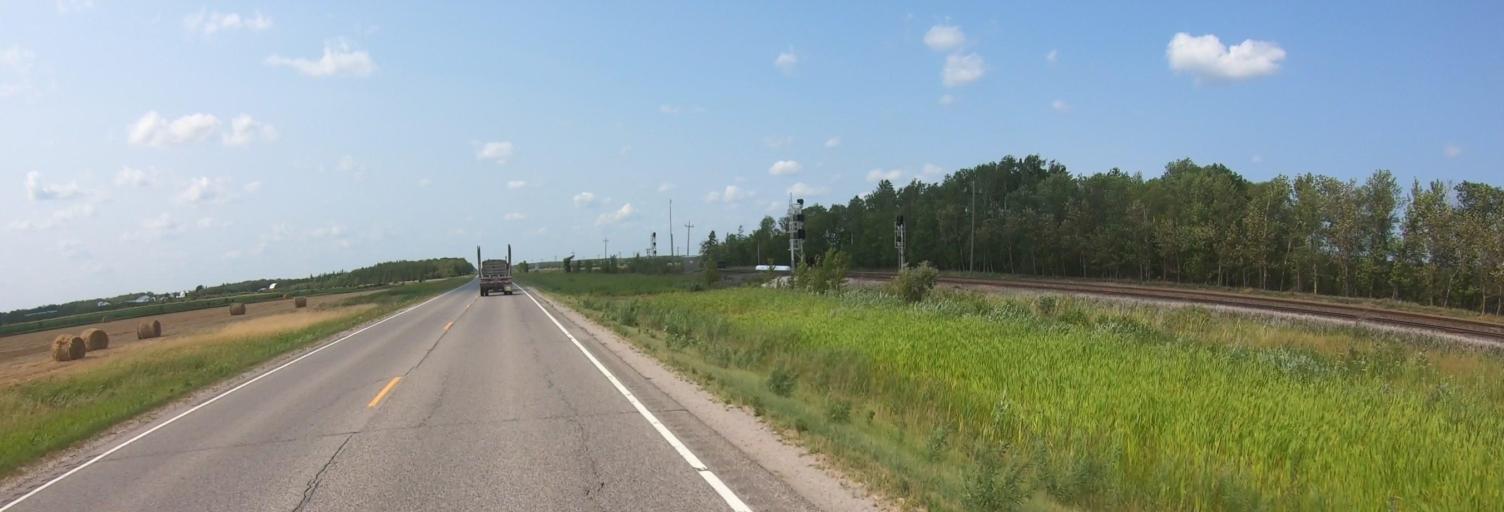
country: US
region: Minnesota
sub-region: Roseau County
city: Warroad
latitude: 48.8560
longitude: -95.2288
